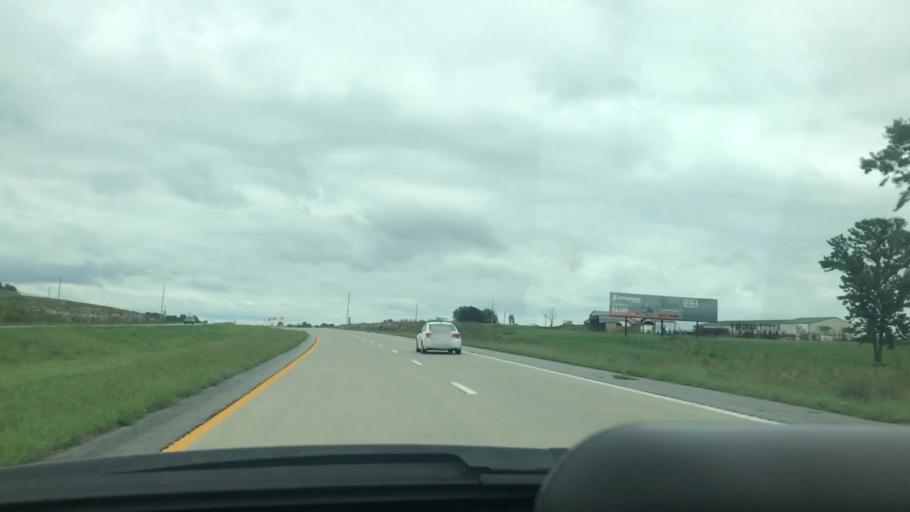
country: US
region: Missouri
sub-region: Dallas County
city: Buffalo
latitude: 37.5945
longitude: -93.1253
